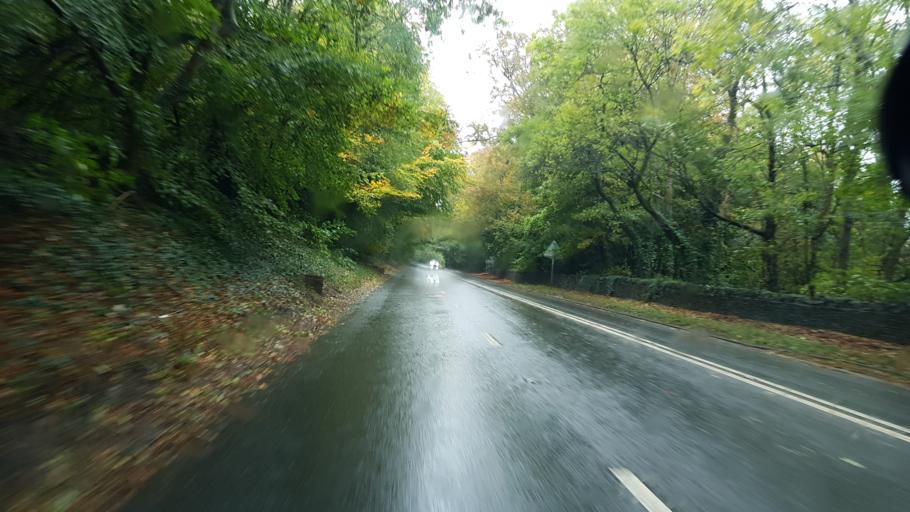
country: GB
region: England
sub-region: Gloucestershire
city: Stow on the Wold
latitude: 51.9193
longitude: -1.7252
